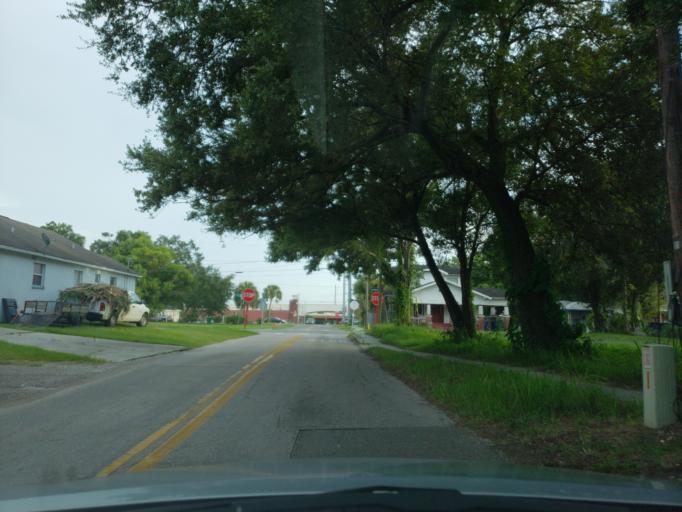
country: US
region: Florida
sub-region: Hillsborough County
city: Tampa
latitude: 27.9679
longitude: -82.4306
